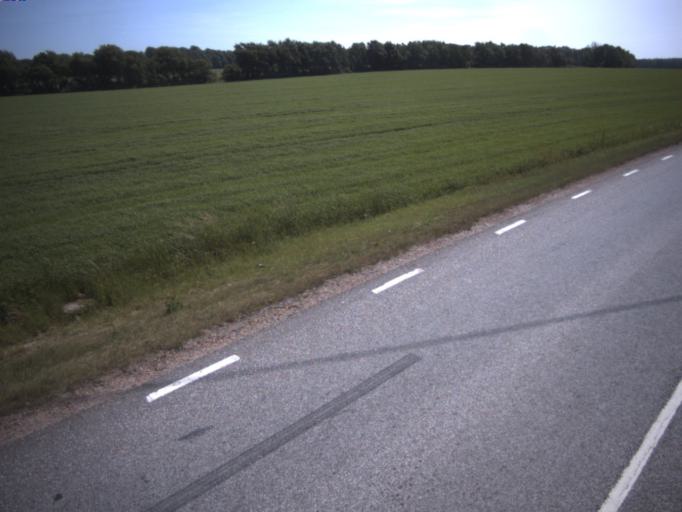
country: SE
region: Skane
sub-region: Helsingborg
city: Helsingborg
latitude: 56.0942
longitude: 12.6797
